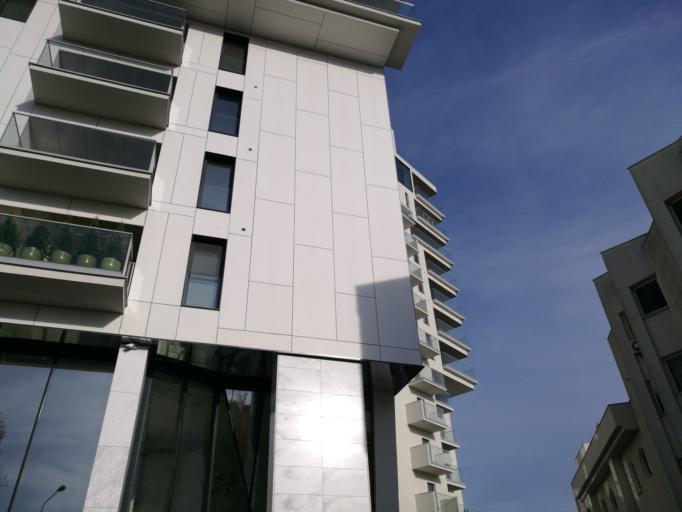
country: RO
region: Bucuresti
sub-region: Municipiul Bucuresti
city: Bucharest
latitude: 44.4769
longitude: 26.0928
